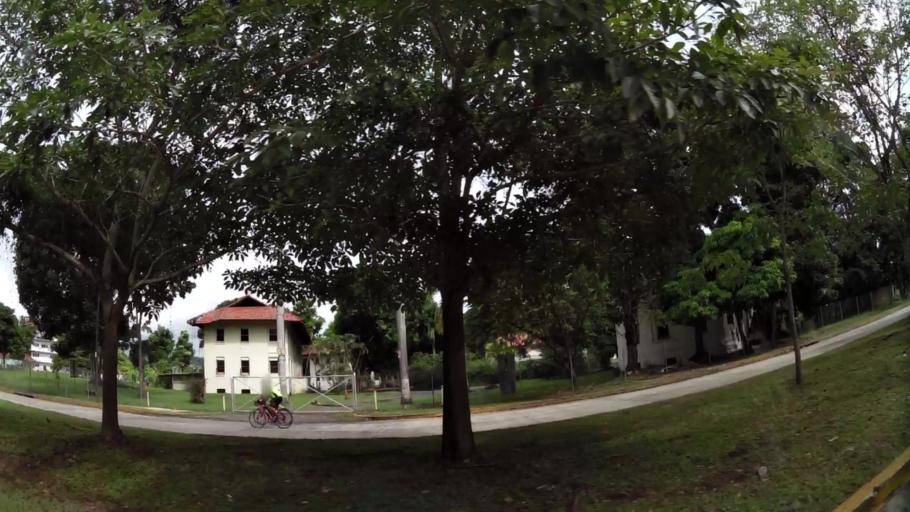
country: PA
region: Panama
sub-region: Distrito de Panama
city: Ancon
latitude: 8.9405
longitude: -79.5505
